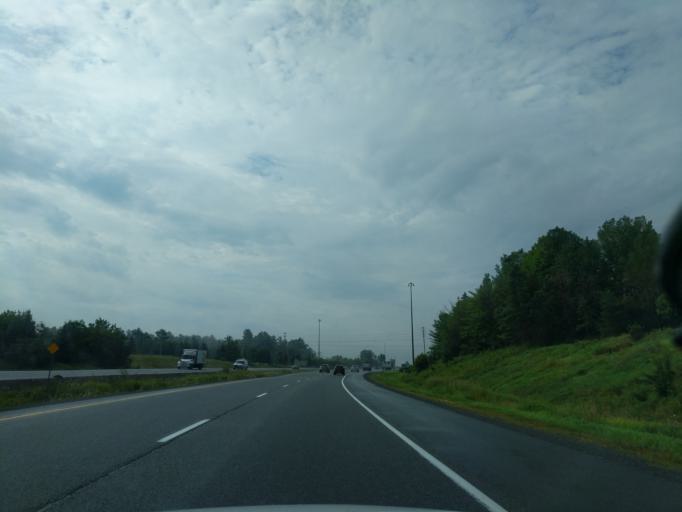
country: CA
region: Ontario
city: Bells Corners
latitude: 45.3256
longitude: -75.8063
